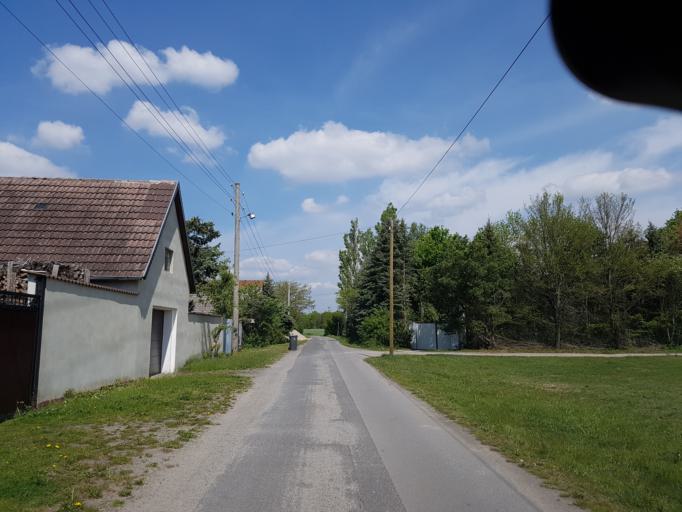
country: DE
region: Brandenburg
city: Finsterwalde
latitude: 51.5696
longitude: 13.6629
